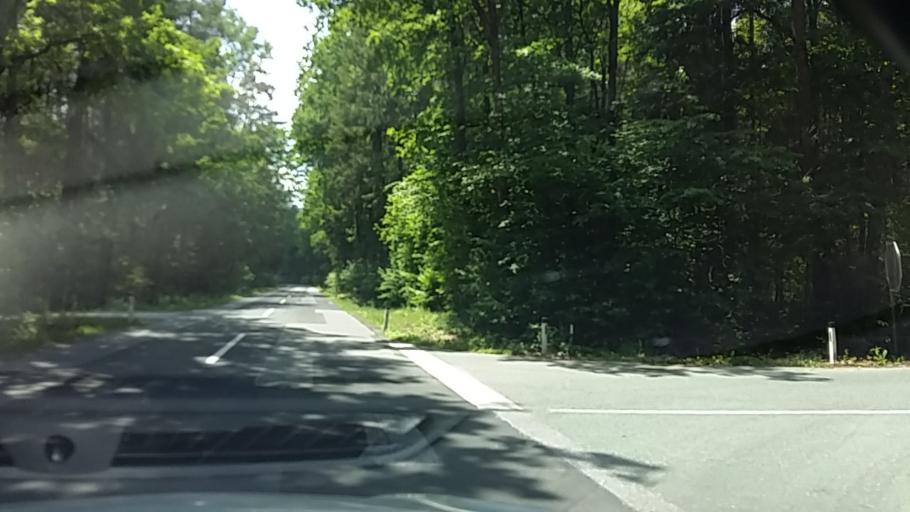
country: AT
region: Styria
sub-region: Politischer Bezirk Hartberg-Fuerstenfeld
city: Burgau
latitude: 47.1196
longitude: 16.0941
